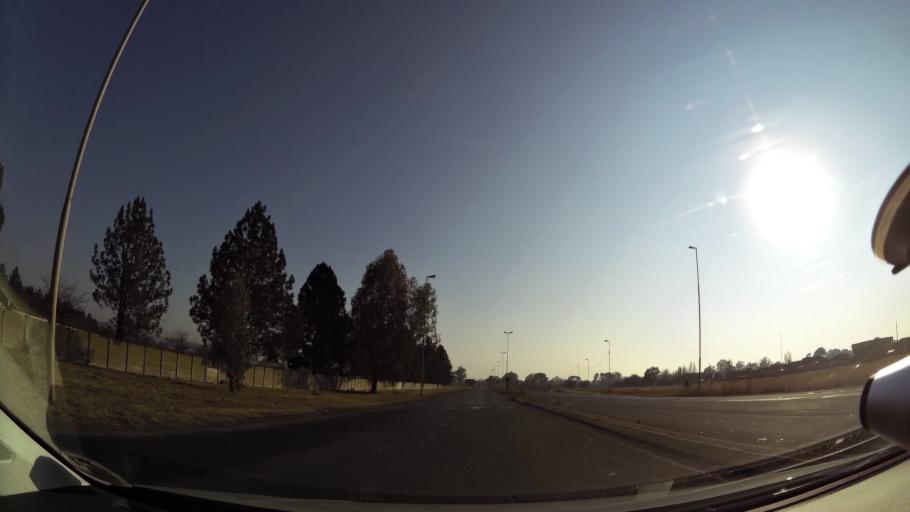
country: ZA
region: Orange Free State
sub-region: Mangaung Metropolitan Municipality
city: Bloemfontein
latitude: -29.1405
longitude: 26.2666
